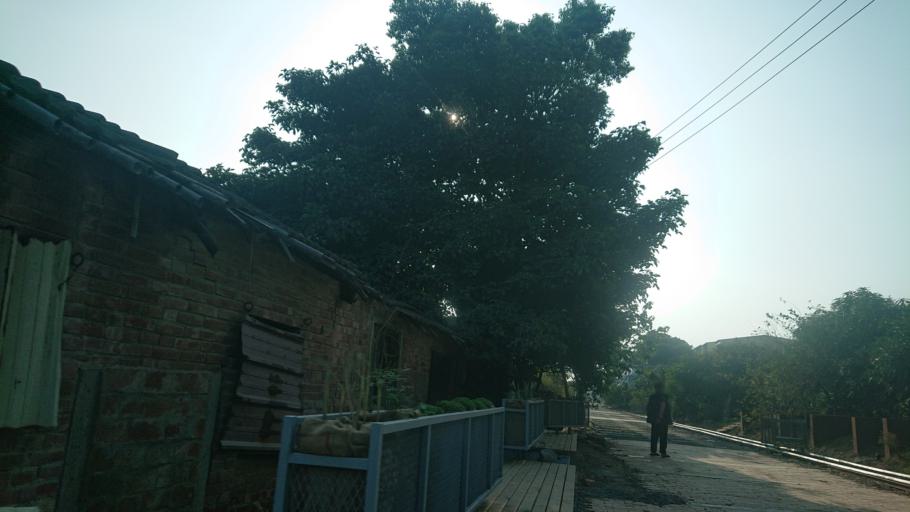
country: TW
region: Taiwan
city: Xinying
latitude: 23.1763
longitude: 120.2599
